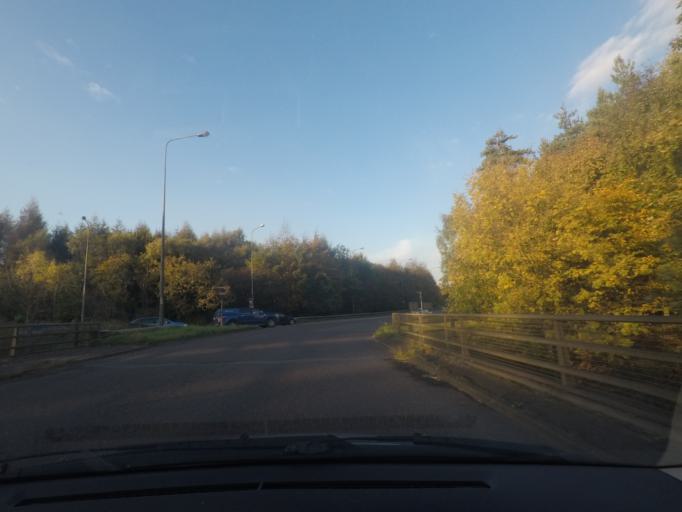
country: GB
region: England
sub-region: North Lincolnshire
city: Scawby
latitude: 53.5446
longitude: -0.5587
